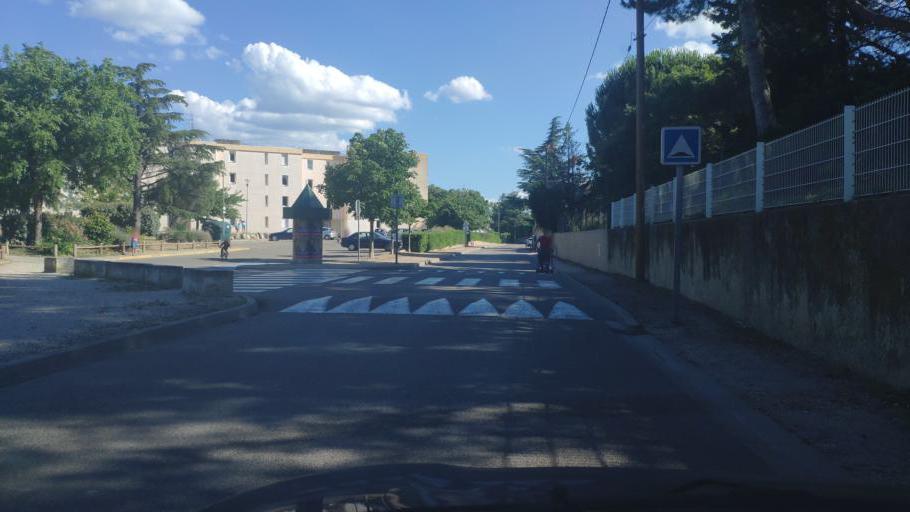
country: FR
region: Provence-Alpes-Cote d'Azur
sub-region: Departement du Vaucluse
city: Entraigues-sur-la-Sorgue
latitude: 43.9988
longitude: 4.9258
